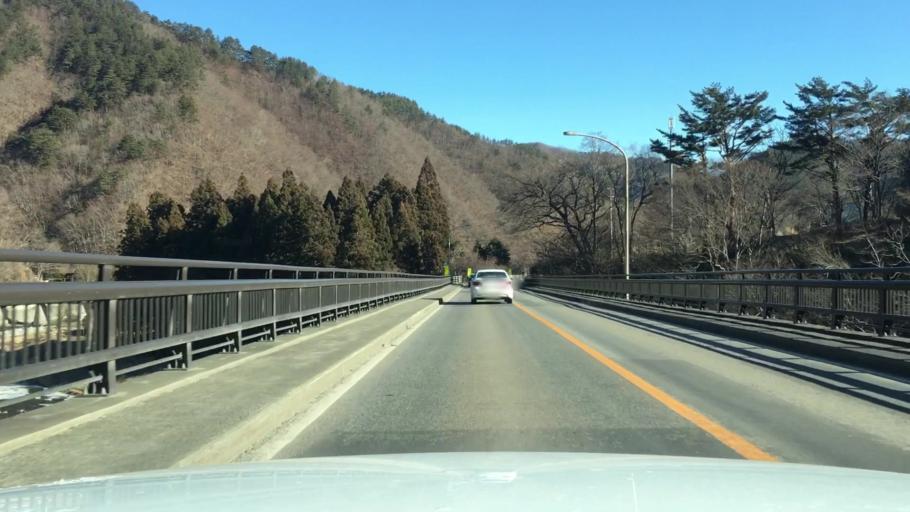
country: JP
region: Iwate
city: Miyako
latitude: 39.6008
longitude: 141.7621
